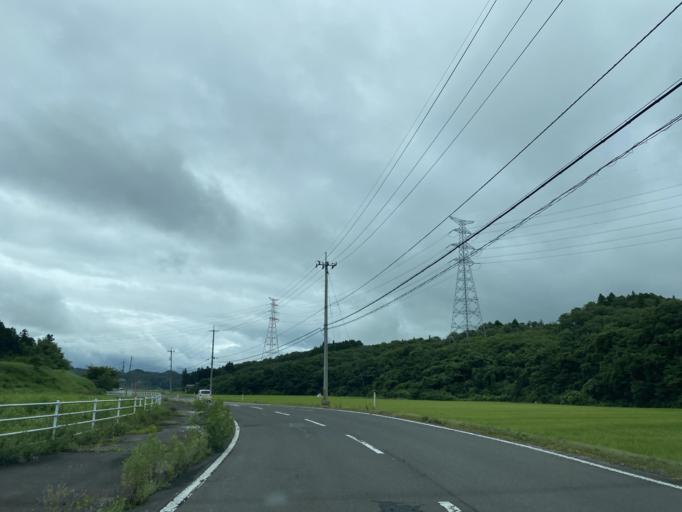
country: JP
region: Miyagi
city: Tomiya
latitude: 38.3867
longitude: 140.9247
